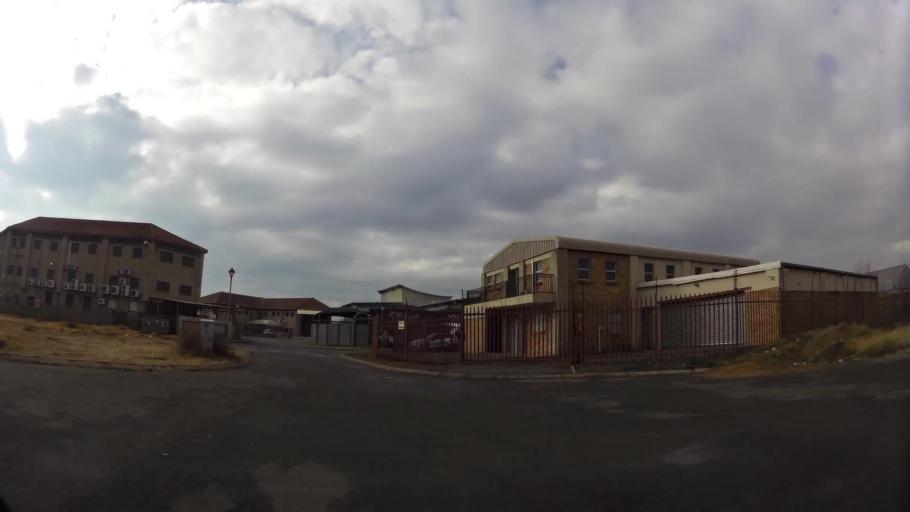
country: ZA
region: Gauteng
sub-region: Sedibeng District Municipality
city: Vanderbijlpark
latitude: -26.6947
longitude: 27.8317
